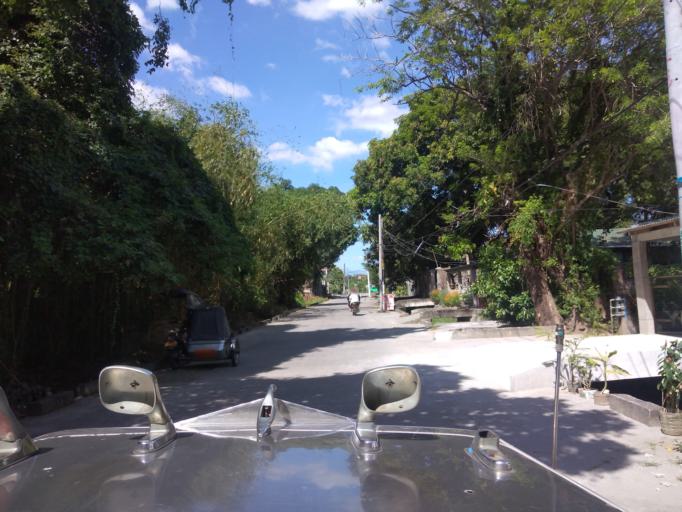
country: PH
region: Central Luzon
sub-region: Province of Pampanga
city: Santa Rita
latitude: 15.0044
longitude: 120.5999
